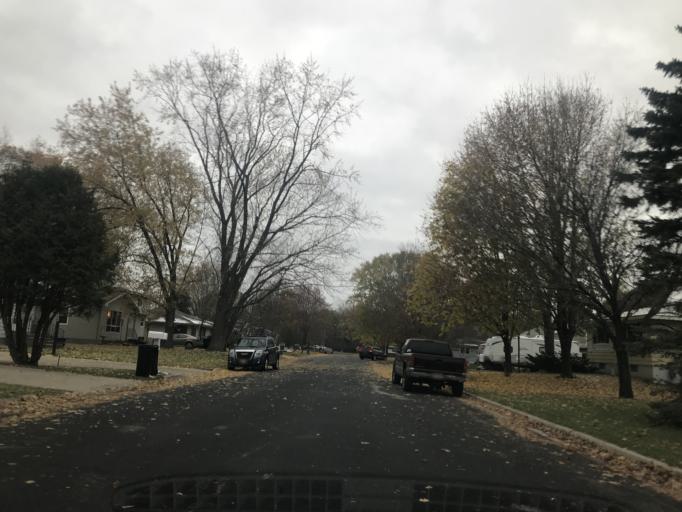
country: US
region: Wisconsin
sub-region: Marinette County
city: Marinette
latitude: 45.0939
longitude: -87.6513
